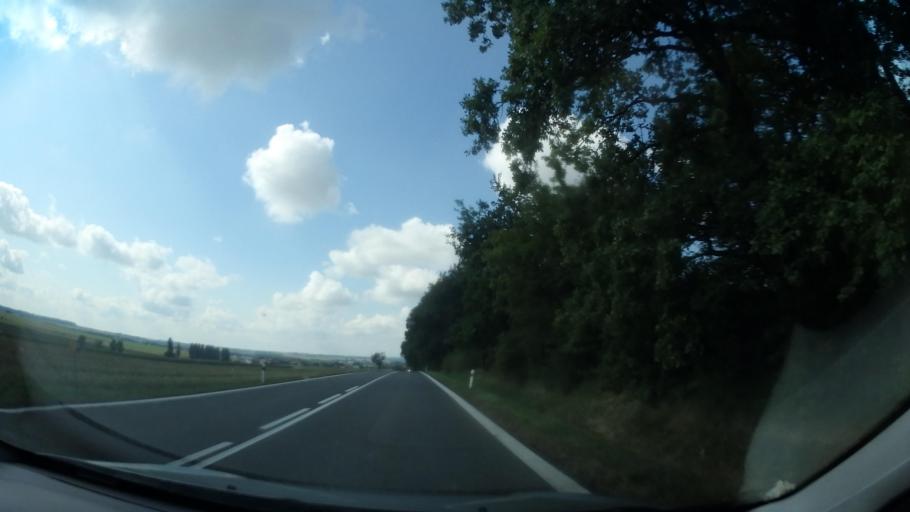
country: CZ
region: Central Bohemia
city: Suchdol
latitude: 49.9565
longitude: 15.1184
